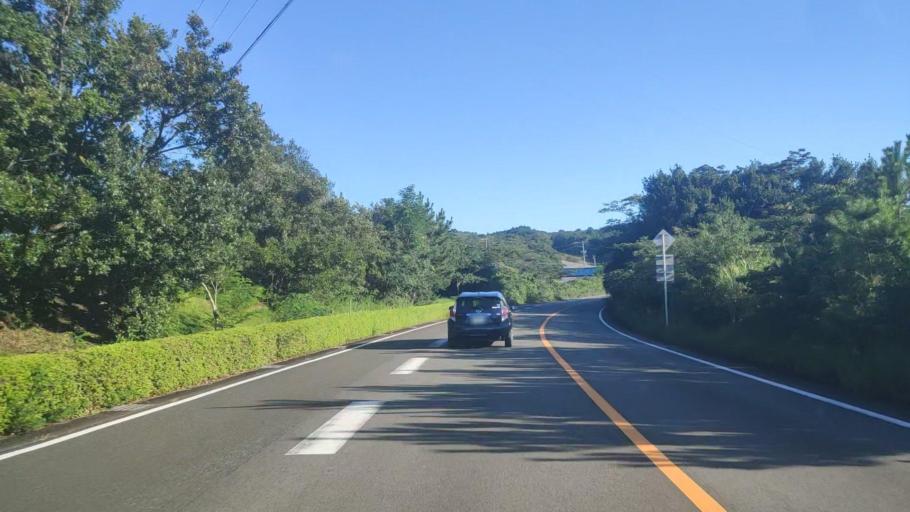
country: JP
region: Mie
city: Toba
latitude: 34.3540
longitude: 136.8454
